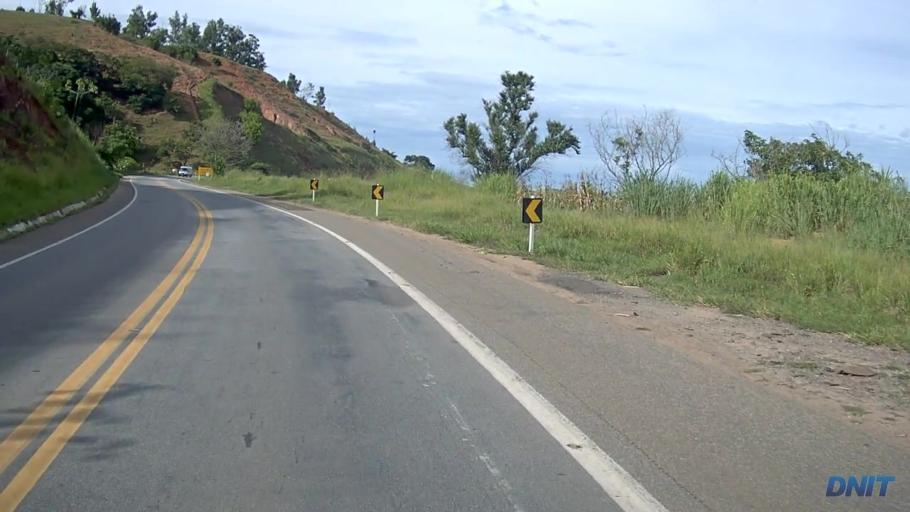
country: BR
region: Minas Gerais
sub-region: Belo Oriente
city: Belo Oriente
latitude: -19.1637
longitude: -42.2418
